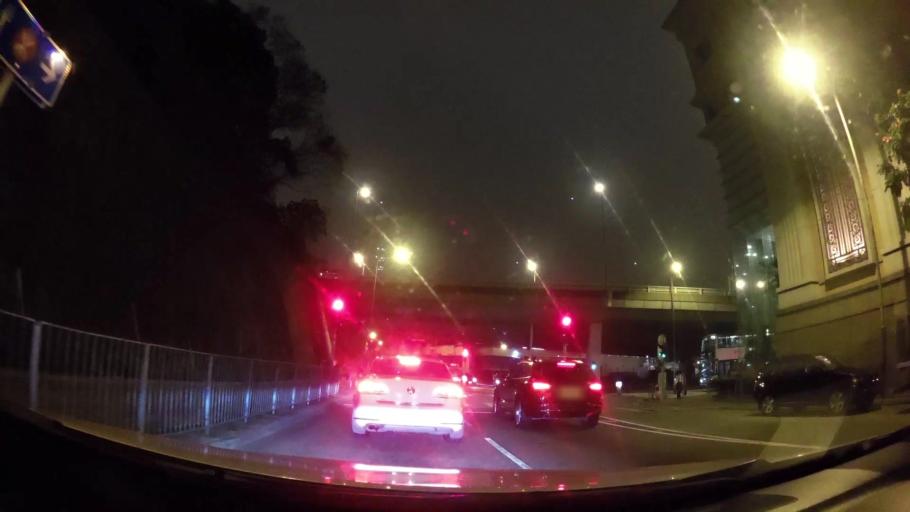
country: HK
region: Sham Shui Po
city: Sham Shui Po
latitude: 22.3418
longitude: 114.1382
